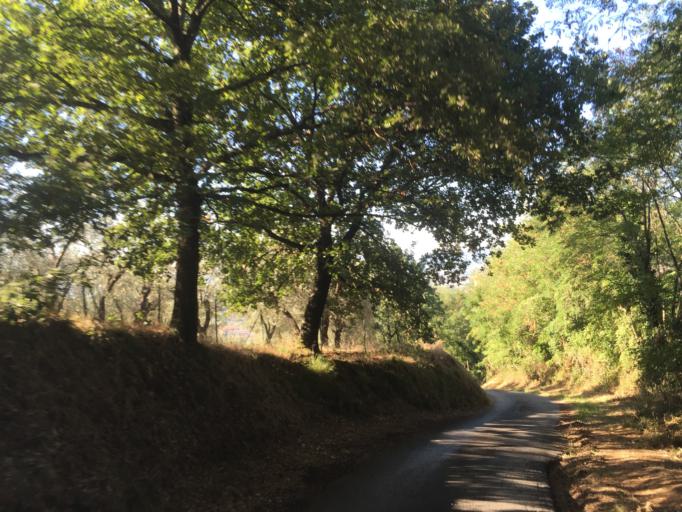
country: IT
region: Tuscany
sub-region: Provincia di Pistoia
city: Pistoia
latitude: 43.9589
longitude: 10.9406
